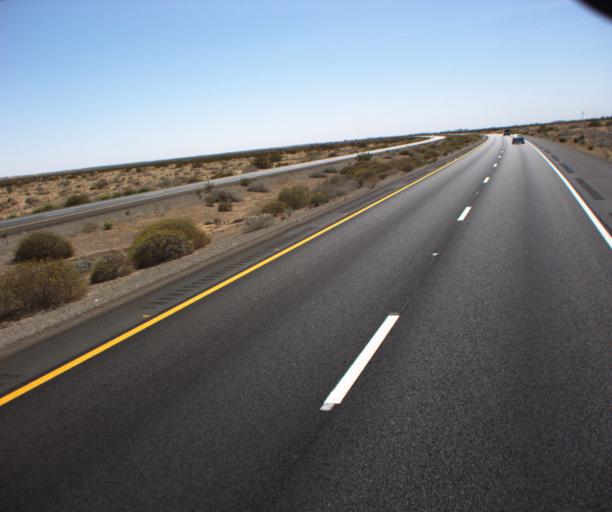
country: US
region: Arizona
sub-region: Yuma County
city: Fortuna Foothills
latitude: 32.6015
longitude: -114.5394
